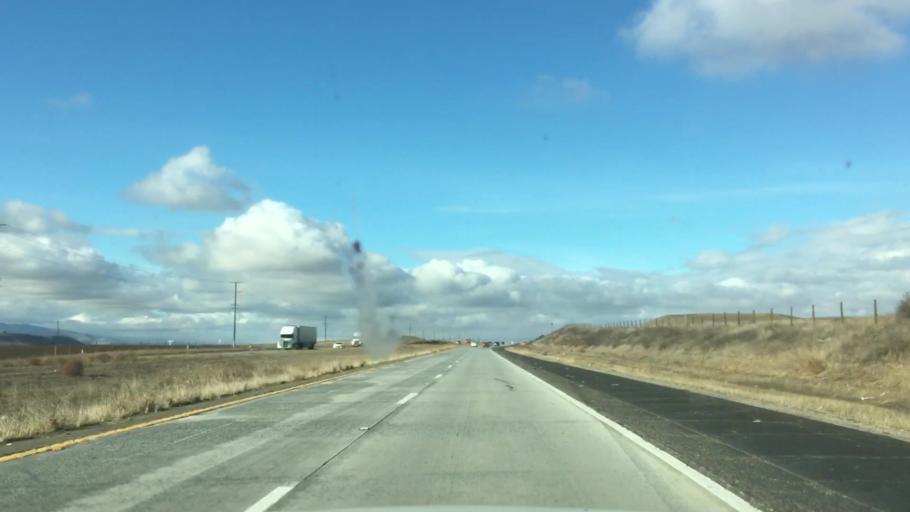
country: US
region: California
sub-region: Monterey County
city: King City
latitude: 36.1386
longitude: -121.0346
